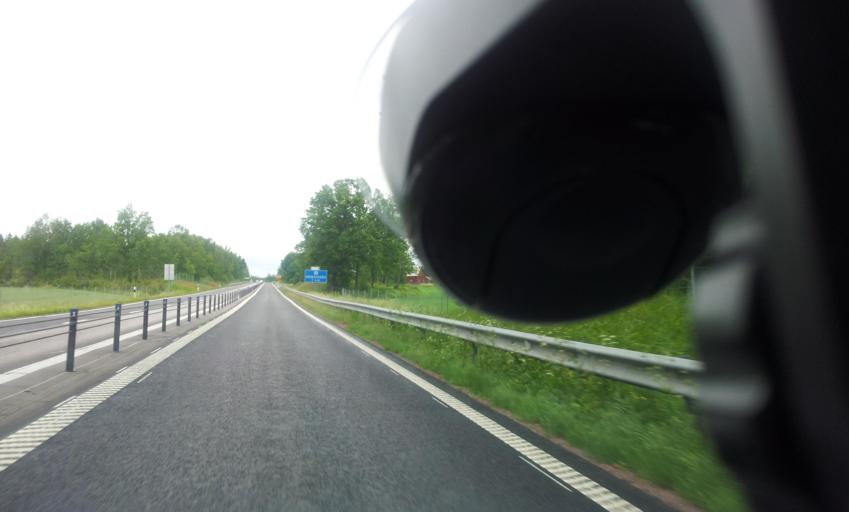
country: SE
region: Kalmar
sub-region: Monsteras Kommun
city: Timmernabben
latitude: 56.9084
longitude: 16.3812
